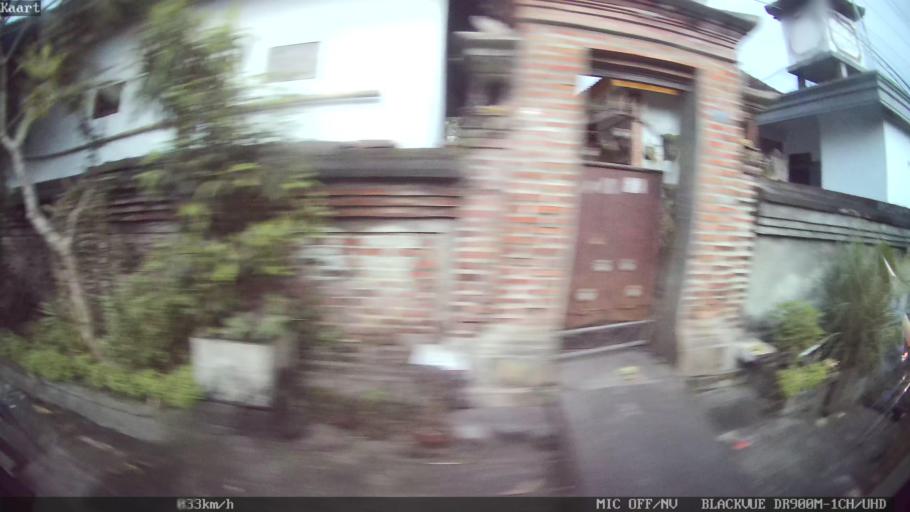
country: ID
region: Bali
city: Banjar Tebongkang
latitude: -8.5273
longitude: 115.2486
